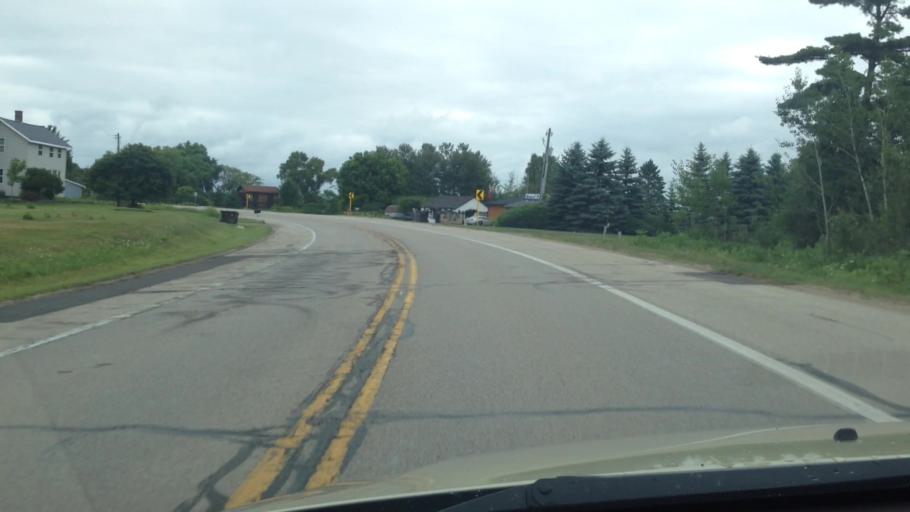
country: US
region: Michigan
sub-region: Delta County
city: Escanaba
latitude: 45.6876
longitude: -87.1025
